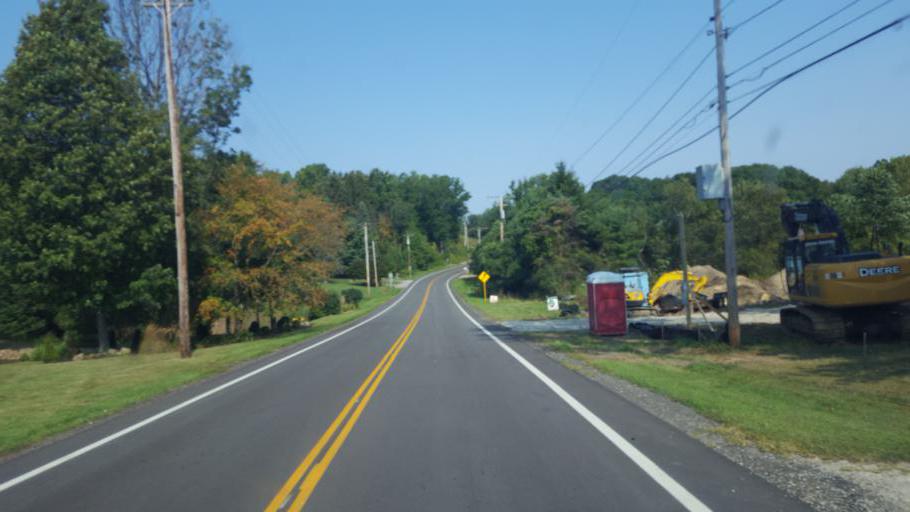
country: US
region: Ohio
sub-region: Lake County
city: Painesville
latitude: 41.6976
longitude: -81.2365
